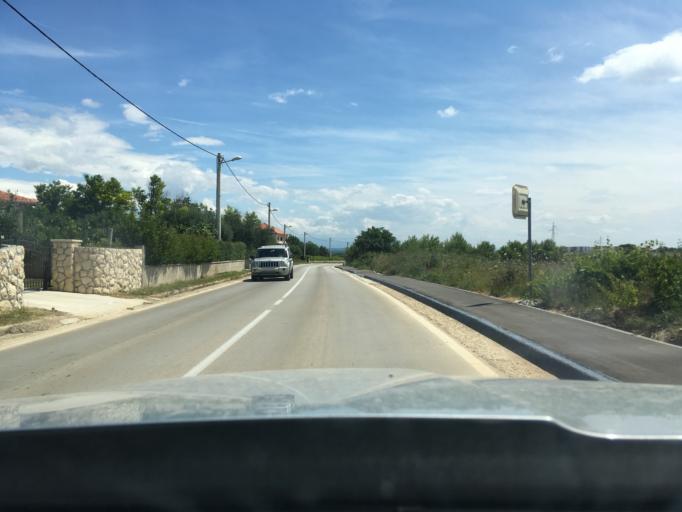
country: HR
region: Zadarska
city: Nin
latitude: 44.2464
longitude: 15.1586
